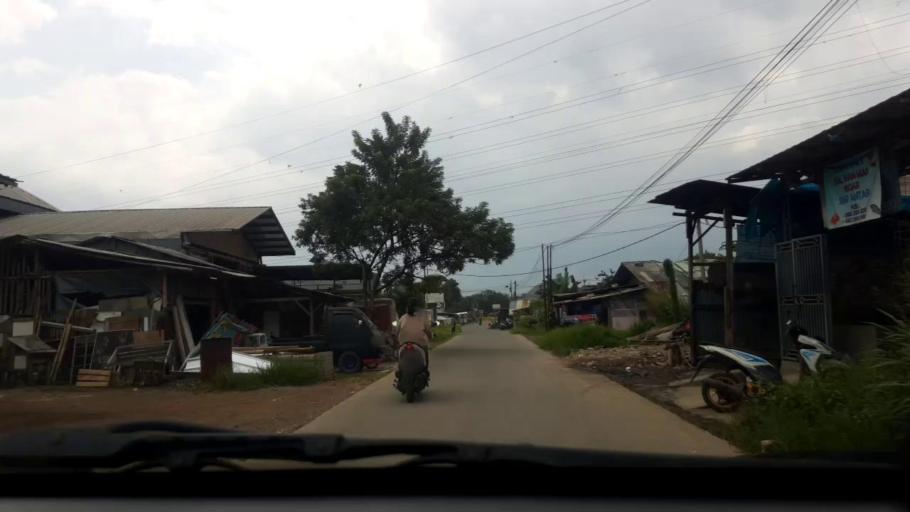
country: ID
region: West Java
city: Cileunyi
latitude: -6.9473
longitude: 107.7210
